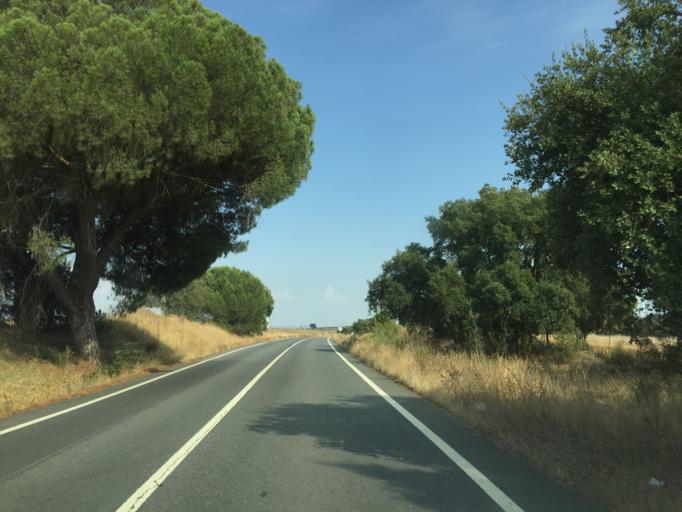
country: PT
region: Beja
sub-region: Aljustrel
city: Aljustrel
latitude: 37.9342
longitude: -8.3539
